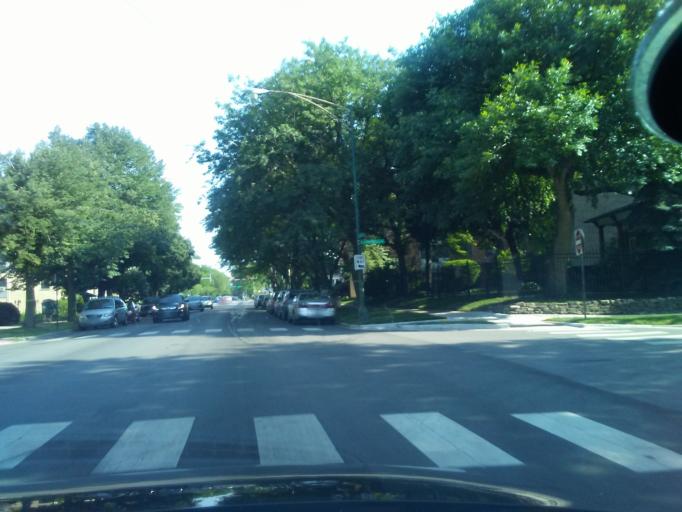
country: US
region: Illinois
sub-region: Cook County
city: Evanston
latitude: 42.0065
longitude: -87.6808
